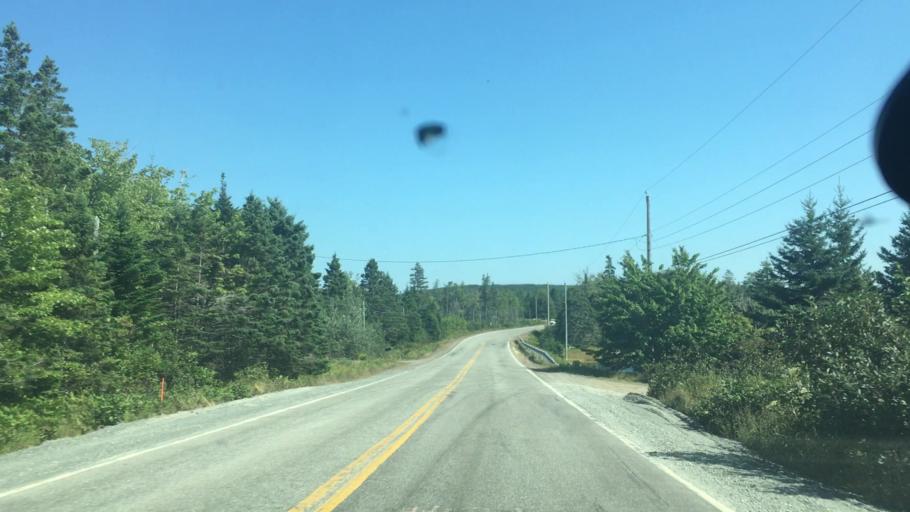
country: CA
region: Nova Scotia
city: New Glasgow
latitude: 44.9000
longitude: -62.4179
